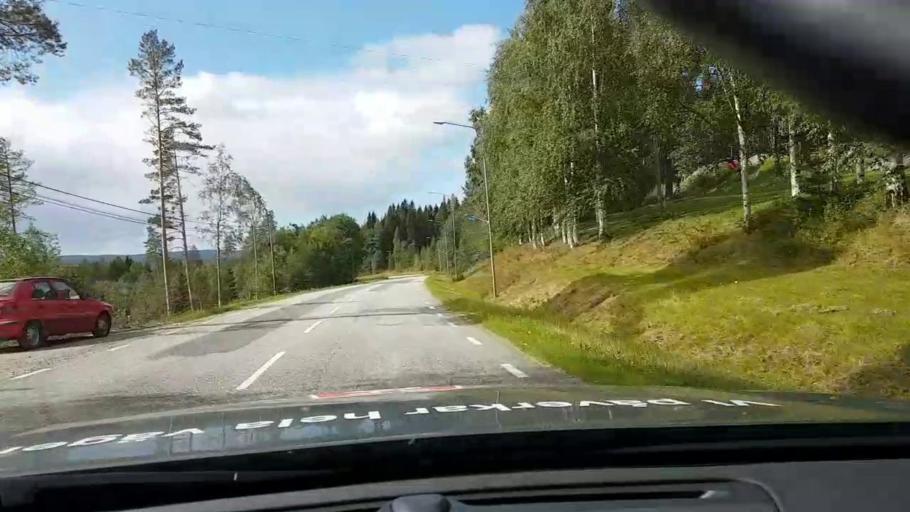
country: SE
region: Vaesterbotten
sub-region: Asele Kommun
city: Asele
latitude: 63.7912
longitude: 17.6242
